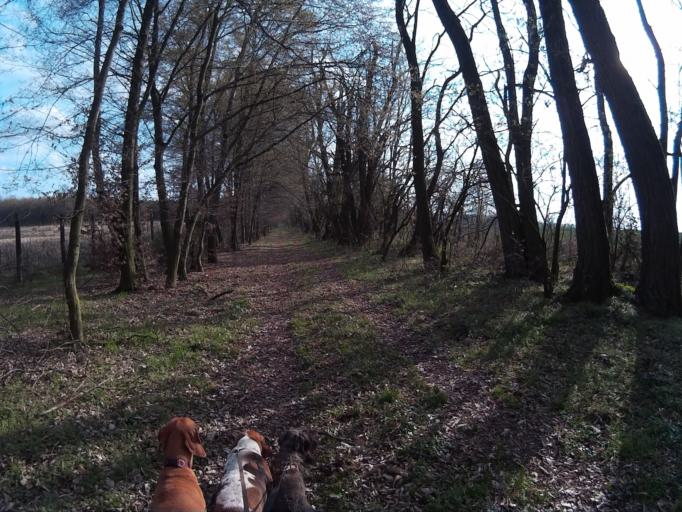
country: HU
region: Vas
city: Sarvar
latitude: 47.2043
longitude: 16.9860
